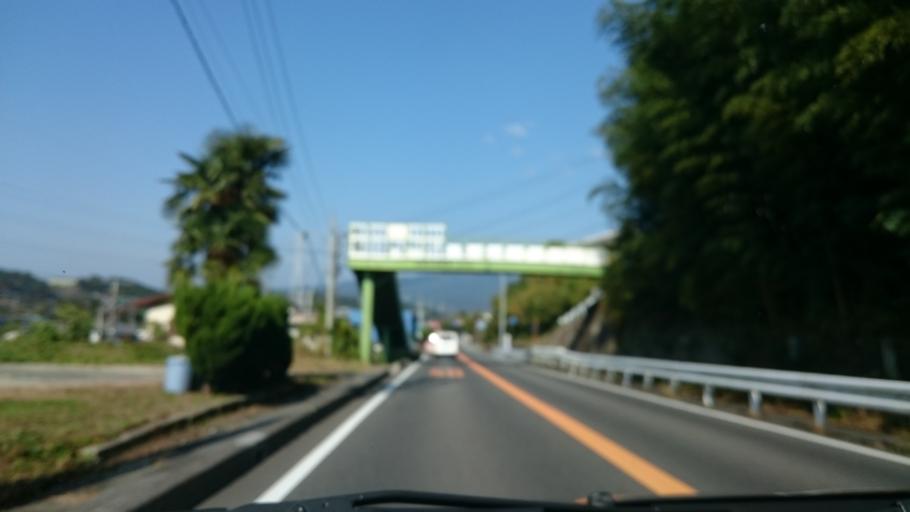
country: JP
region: Gifu
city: Nakatsugawa
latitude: 35.4861
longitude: 137.4874
